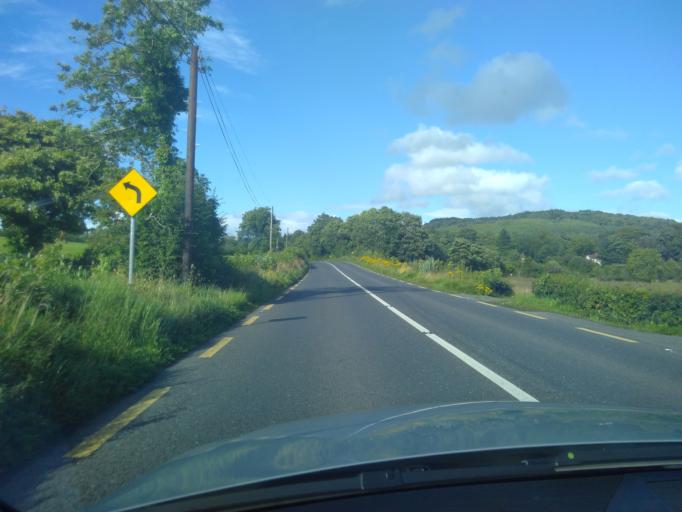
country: IE
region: Ulster
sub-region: County Donegal
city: Ballybofey
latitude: 54.8217
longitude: -7.7545
